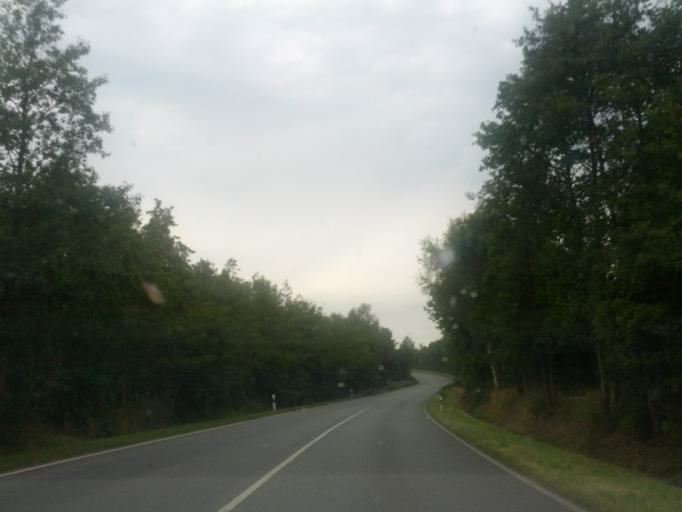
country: DE
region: Mecklenburg-Vorpommern
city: Kropelin
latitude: 54.0748
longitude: 11.8042
